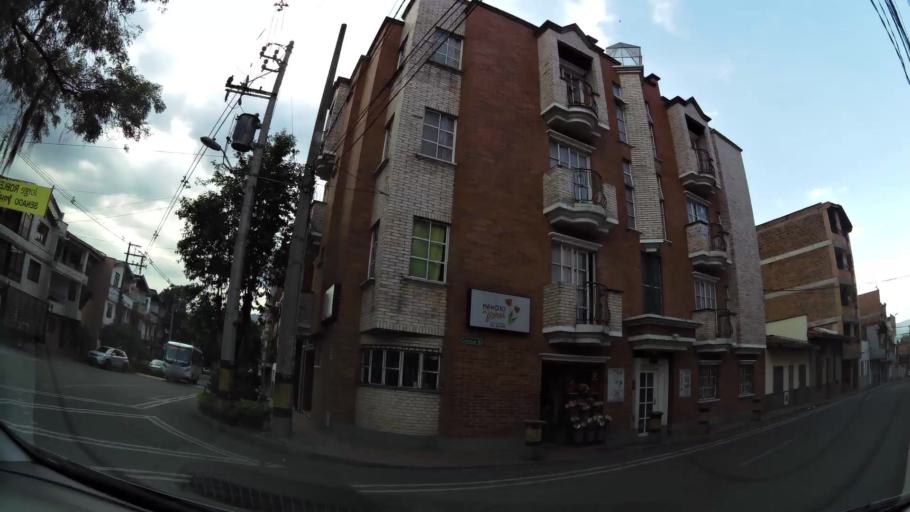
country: CO
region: Antioquia
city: Envigado
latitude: 6.1644
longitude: -75.5833
